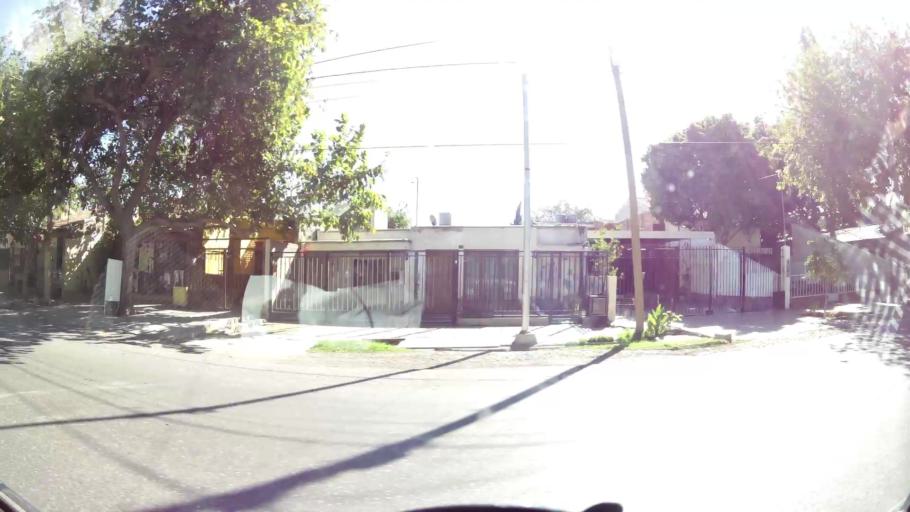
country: AR
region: San Juan
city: San Juan
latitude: -31.5224
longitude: -68.5367
